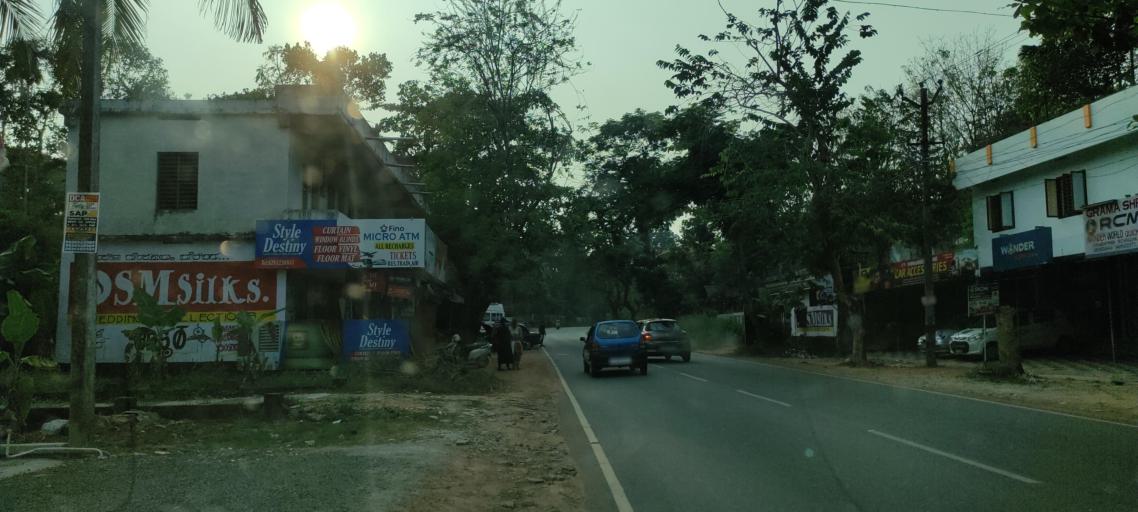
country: IN
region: Kerala
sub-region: Pattanamtitta
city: Adur
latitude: 9.1648
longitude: 76.6913
